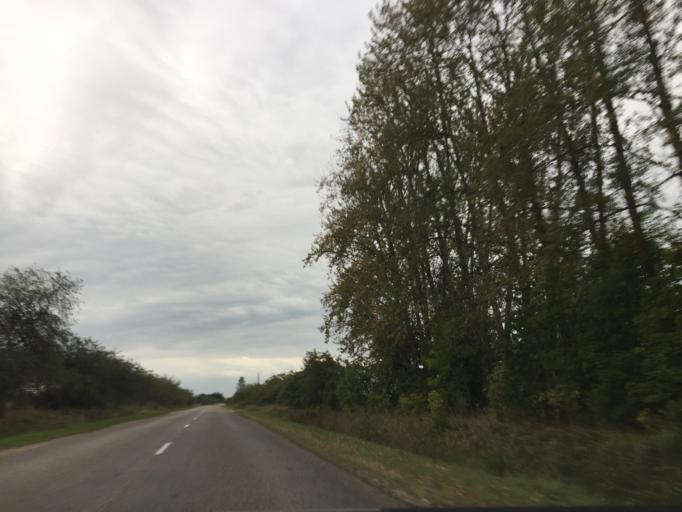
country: LV
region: Krimulda
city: Ragana
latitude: 57.3111
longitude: 24.6437
